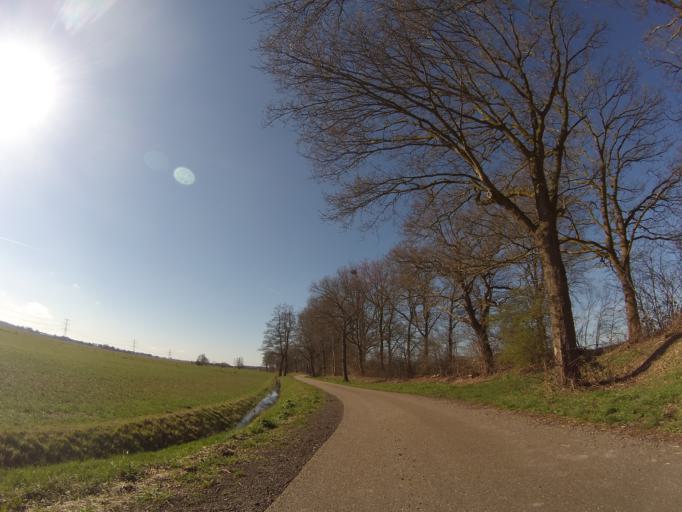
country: NL
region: Drenthe
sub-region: Gemeente Coevorden
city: Sleen
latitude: 52.7484
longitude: 6.8322
